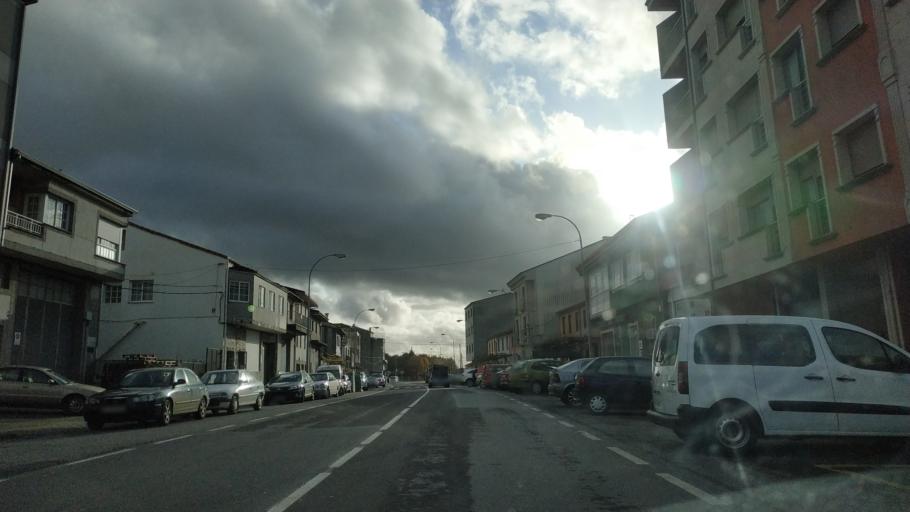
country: ES
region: Galicia
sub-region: Provincia da Coruna
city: Arzua
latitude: 42.9365
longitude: -8.1609
